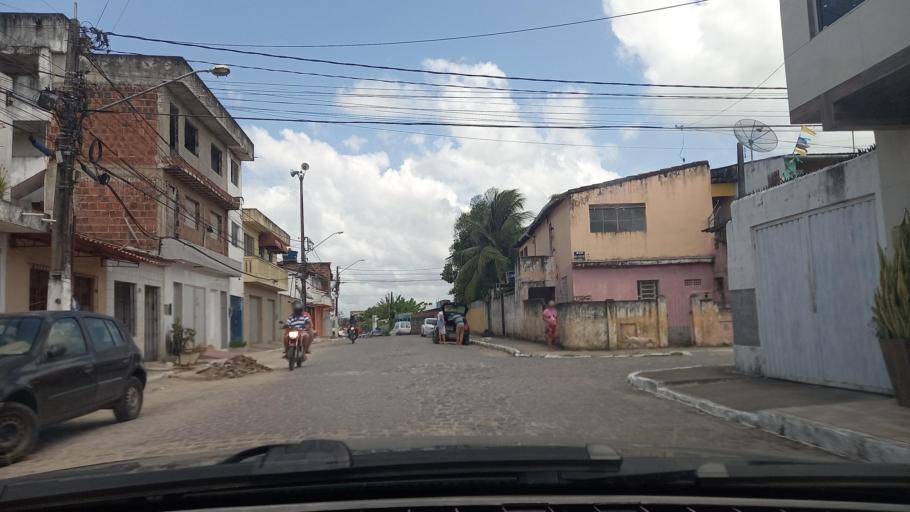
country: BR
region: Pernambuco
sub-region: Goiana
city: Goiana
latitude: -7.5618
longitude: -35.0097
